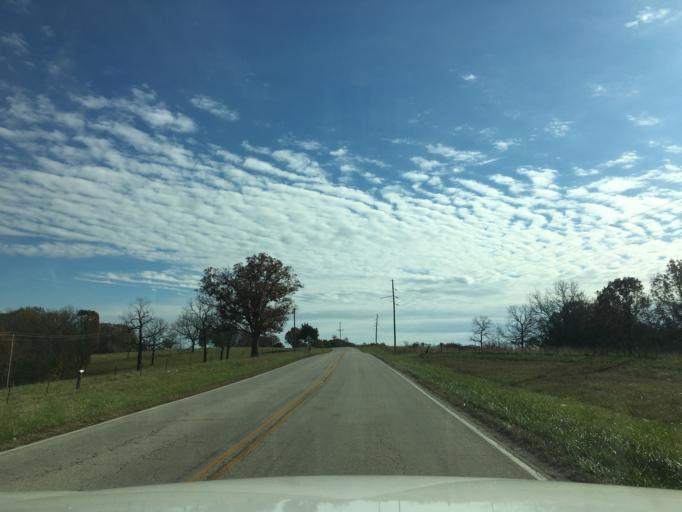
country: US
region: Missouri
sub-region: Osage County
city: Linn
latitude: 38.3774
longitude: -91.8165
